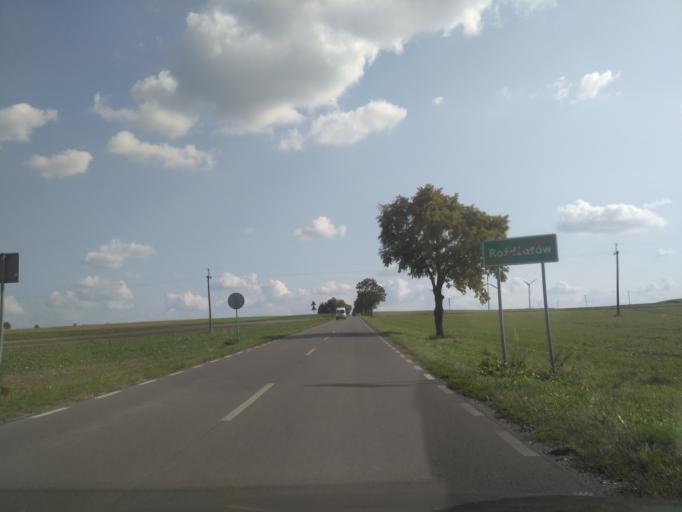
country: PL
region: Lublin Voivodeship
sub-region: Powiat chelmski
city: Pokrowka
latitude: 51.0673
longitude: 23.5175
